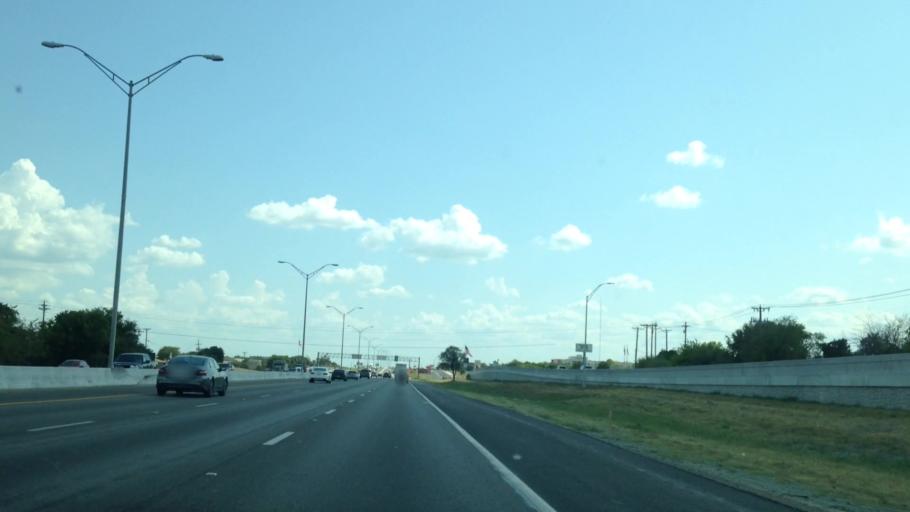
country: US
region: Texas
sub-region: Williamson County
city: Round Rock
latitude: 30.5486
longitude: -97.6926
